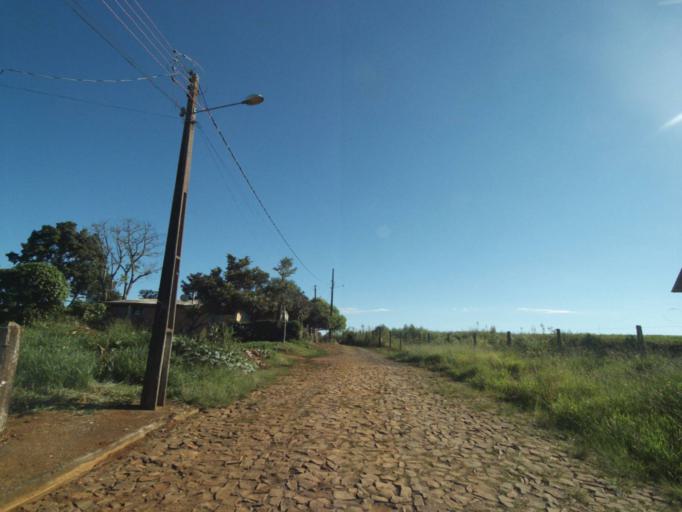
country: BR
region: Parana
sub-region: Pinhao
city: Pinhao
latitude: -25.8333
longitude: -52.0246
